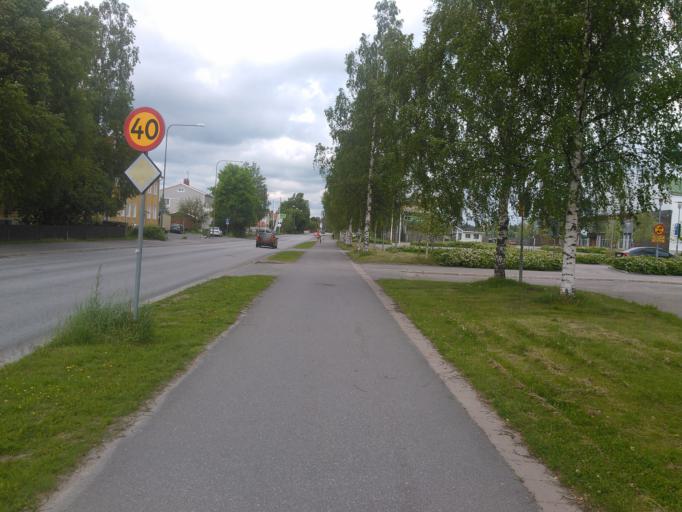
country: SE
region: Vaesterbotten
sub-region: Umea Kommun
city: Umea
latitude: 63.8280
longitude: 20.2850
